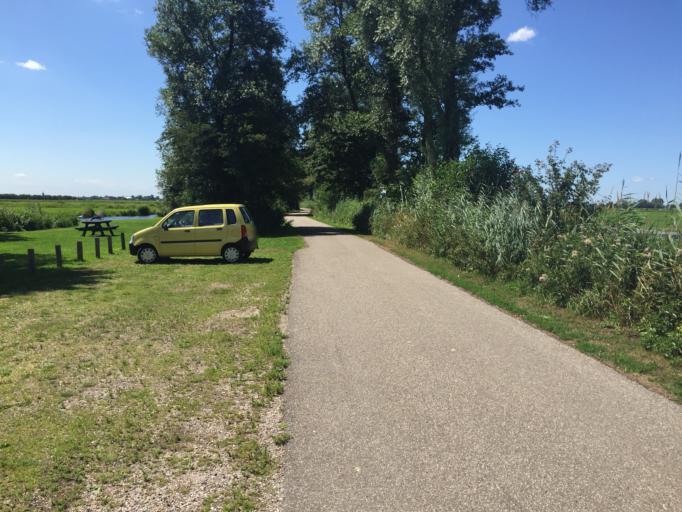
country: NL
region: Utrecht
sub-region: Gemeente Woerden
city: Woerden
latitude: 52.1469
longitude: 4.9223
